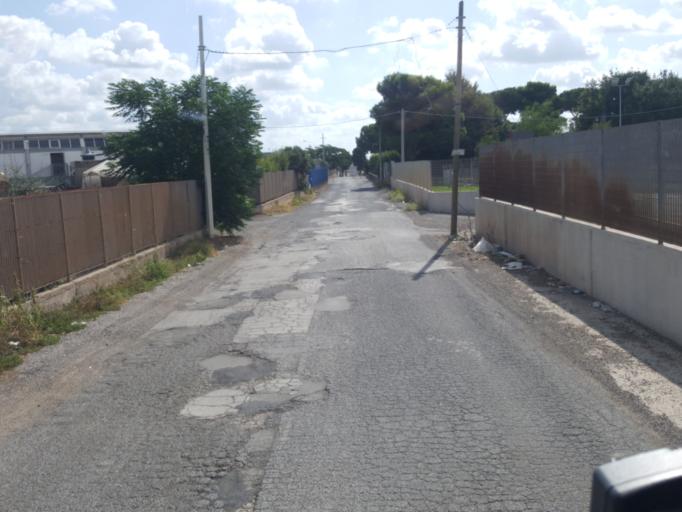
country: IT
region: Latium
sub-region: Citta metropolitana di Roma Capitale
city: Area Produttiva
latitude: 41.6994
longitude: 12.5387
